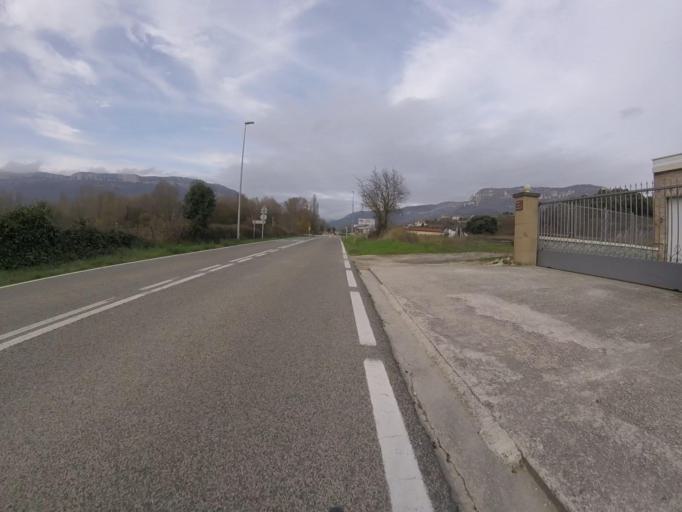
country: ES
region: Navarre
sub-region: Provincia de Navarra
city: Estella
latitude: 42.7131
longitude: -2.0727
